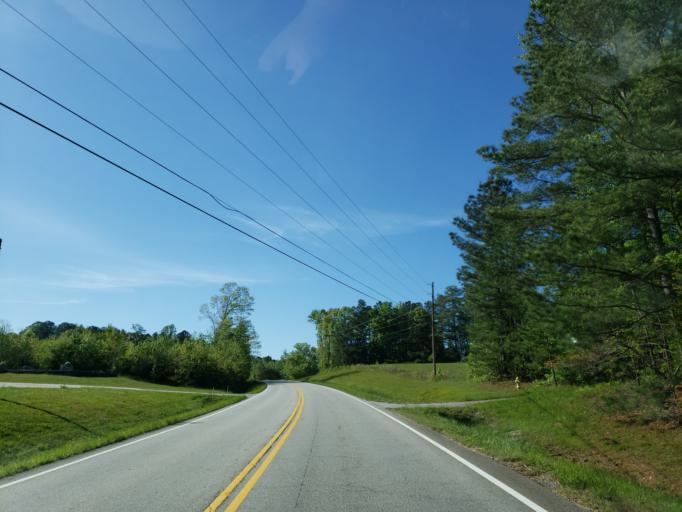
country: US
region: Georgia
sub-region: Haralson County
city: Tallapoosa
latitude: 33.8626
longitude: -85.2942
